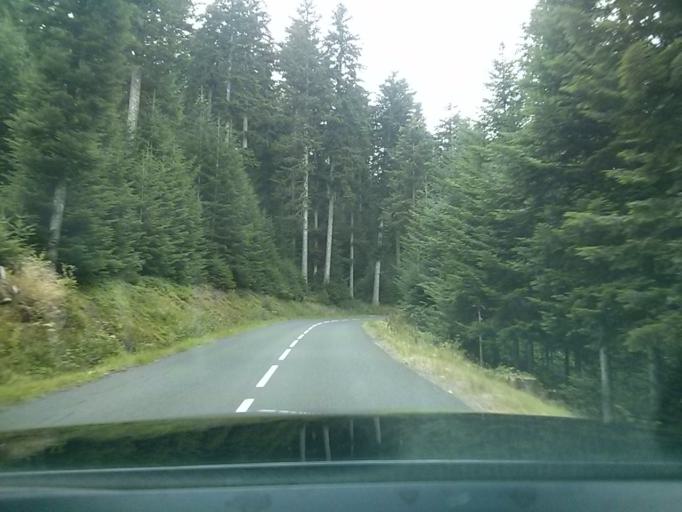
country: FR
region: Rhone-Alpes
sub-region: Departement de la Loire
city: Saint-Genest-Malifaux
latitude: 45.3557
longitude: 4.4783
